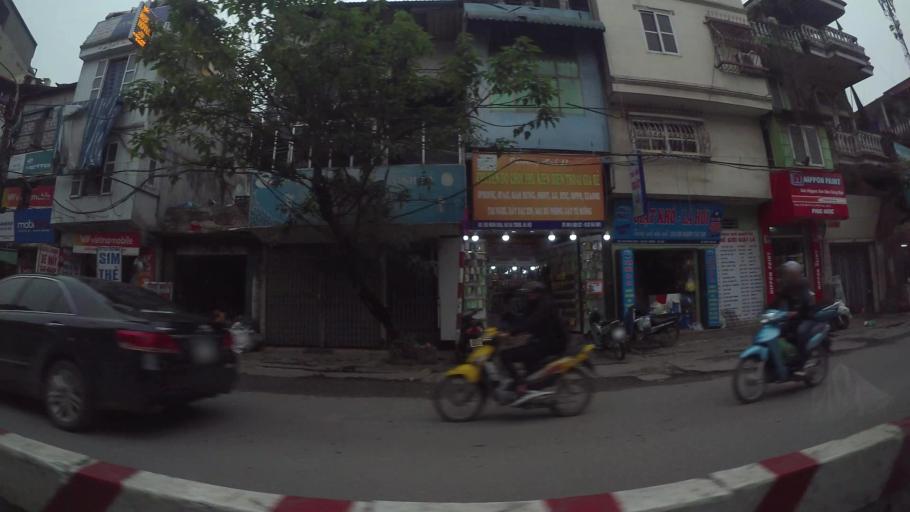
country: VN
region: Ha Noi
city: Hai BaTrung
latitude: 21.0034
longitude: 105.8696
